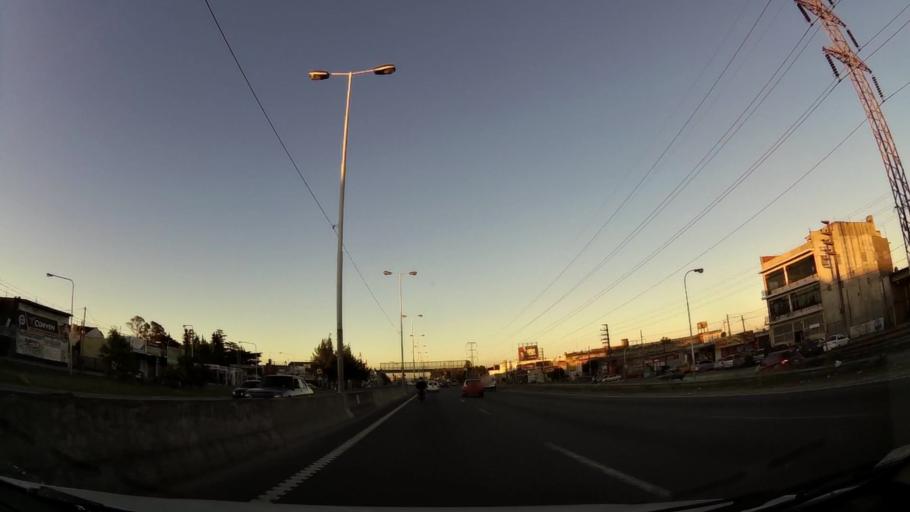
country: AR
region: Buenos Aires
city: Pontevedra
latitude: -34.7715
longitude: -58.6202
